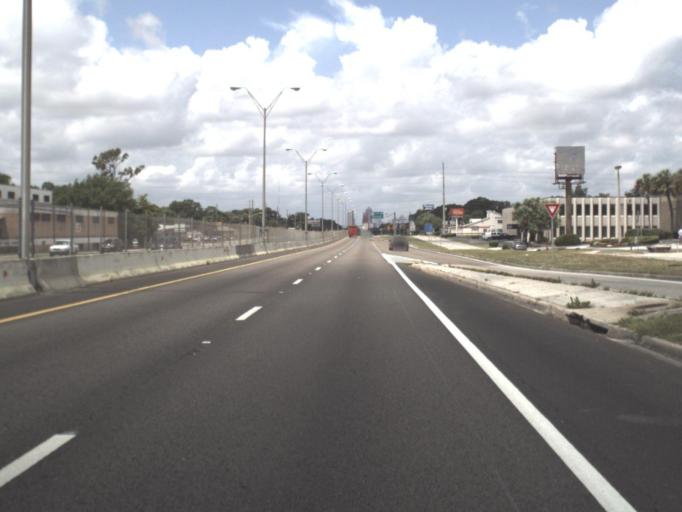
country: US
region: Florida
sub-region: Duval County
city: Jacksonville
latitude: 30.3276
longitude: -81.5883
